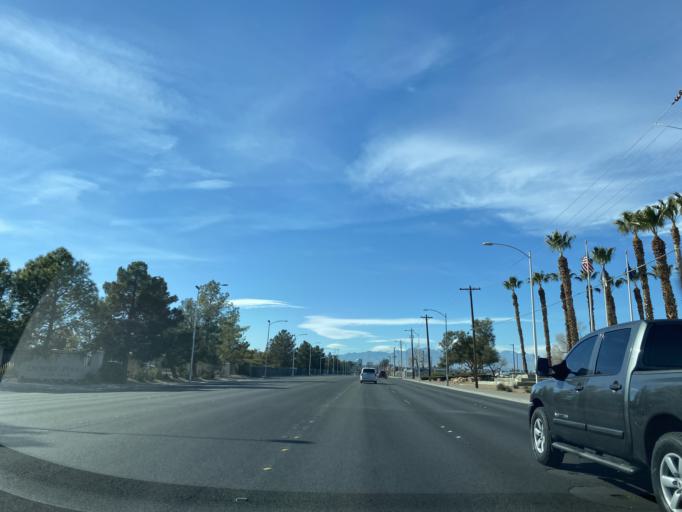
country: US
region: Nevada
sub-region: Clark County
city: North Las Vegas
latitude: 36.1736
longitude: -115.0998
